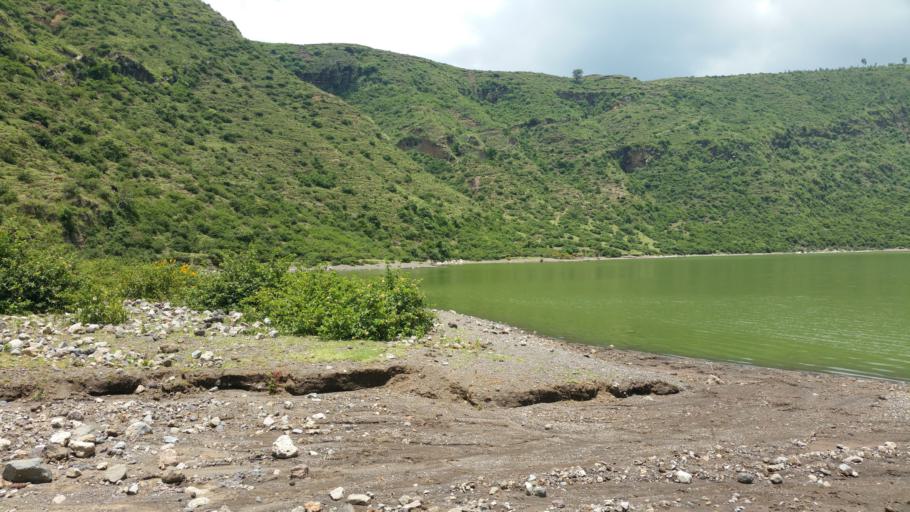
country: ET
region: Oromiya
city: Bishoftu
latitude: 8.6940
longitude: 38.9797
